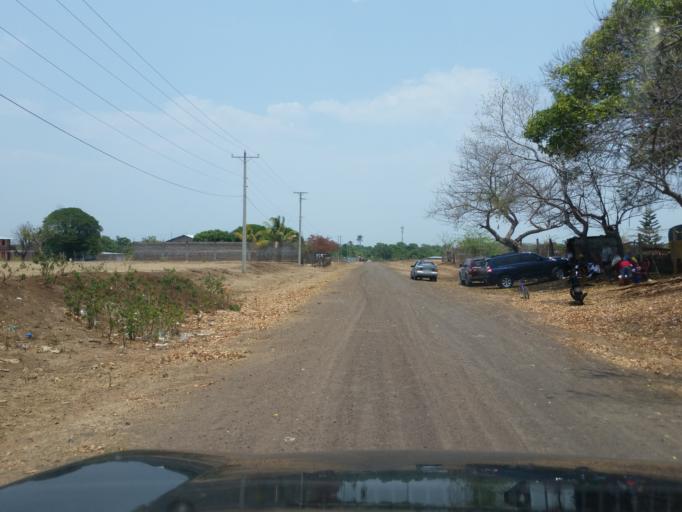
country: NI
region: Granada
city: Granada
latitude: 11.9154
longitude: -85.9630
